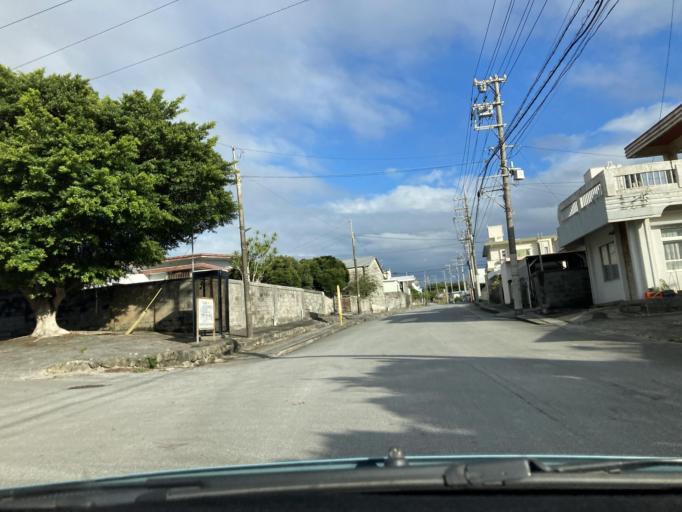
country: JP
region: Okinawa
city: Itoman
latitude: 26.1158
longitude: 127.6769
